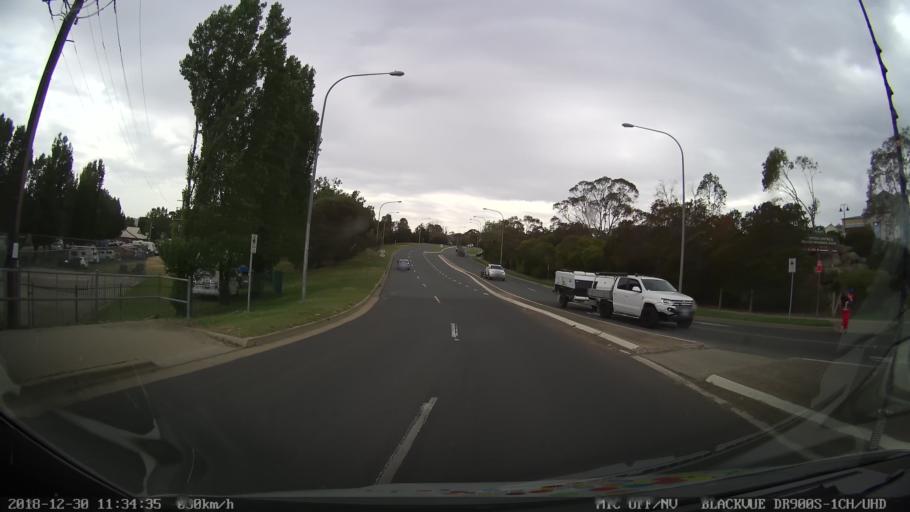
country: AU
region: New South Wales
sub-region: Snowy River
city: Jindabyne
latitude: -36.4148
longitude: 148.6189
